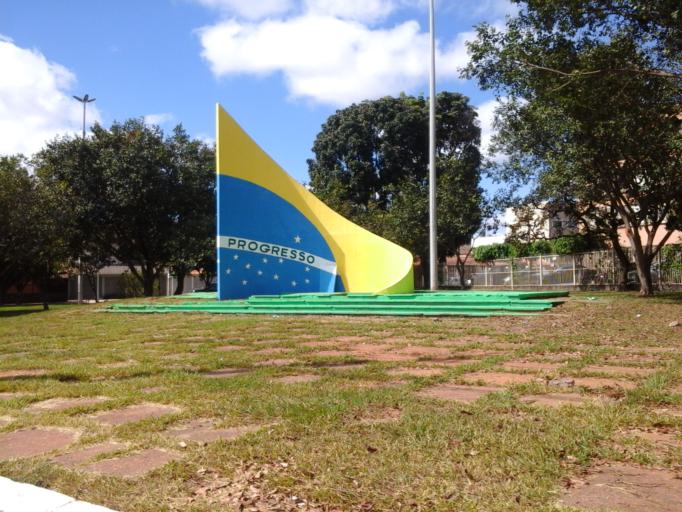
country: BR
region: Federal District
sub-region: Brasilia
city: Brasilia
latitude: -15.8122
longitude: -47.9786
